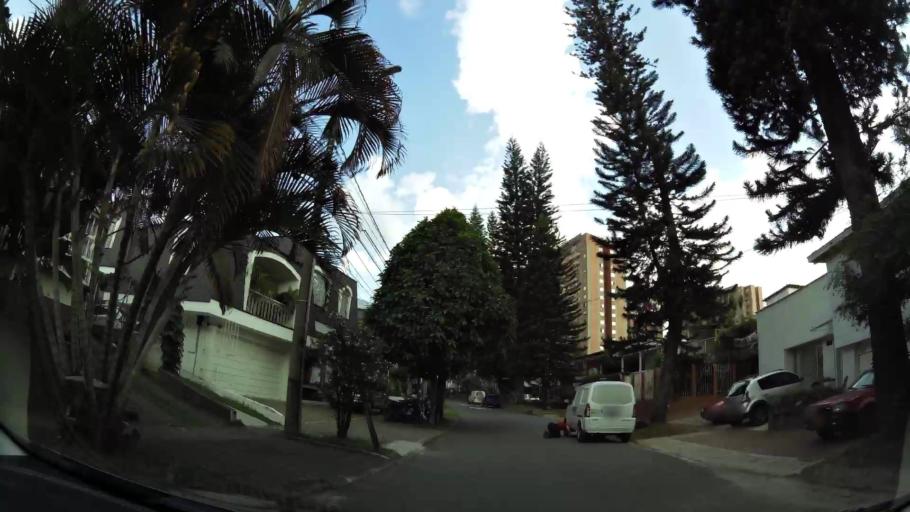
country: CO
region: Antioquia
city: Itagui
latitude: 6.2077
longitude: -75.5756
